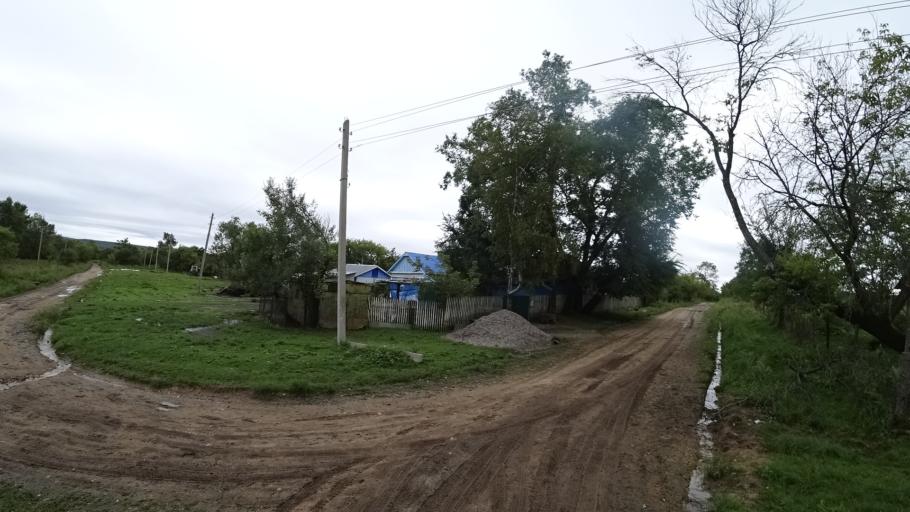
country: RU
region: Primorskiy
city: Rettikhovka
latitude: 44.1364
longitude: 132.6528
